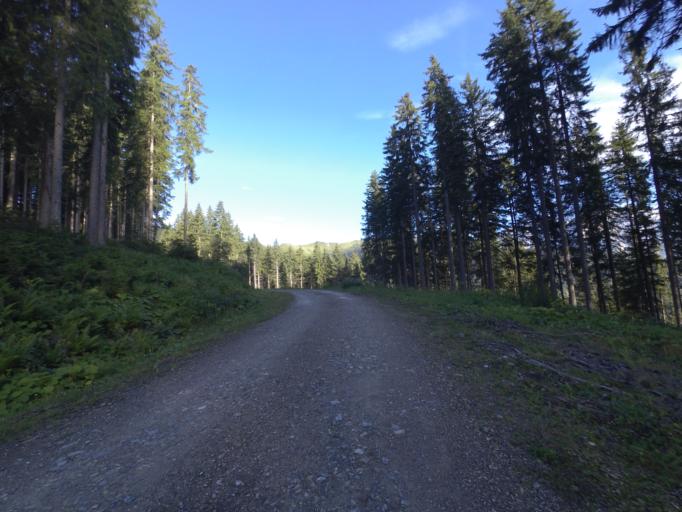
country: AT
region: Salzburg
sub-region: Politischer Bezirk Sankt Johann im Pongau
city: Muhlbach am Hochkonig
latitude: 47.3530
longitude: 13.1038
